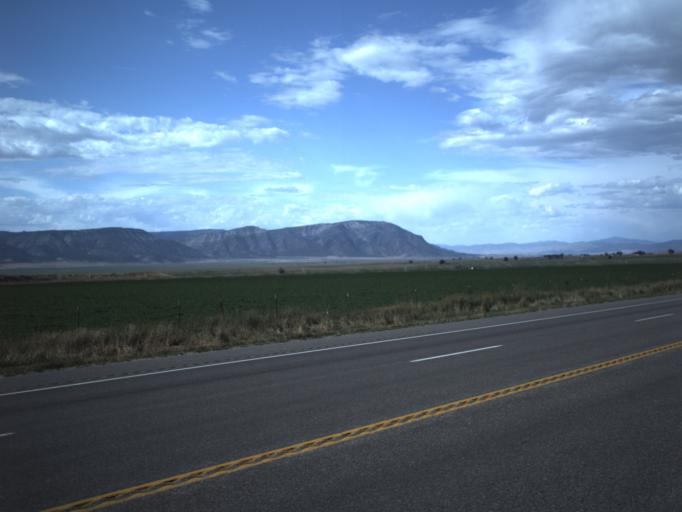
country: US
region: Utah
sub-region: Sanpete County
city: Manti
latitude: 39.2866
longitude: -111.6267
